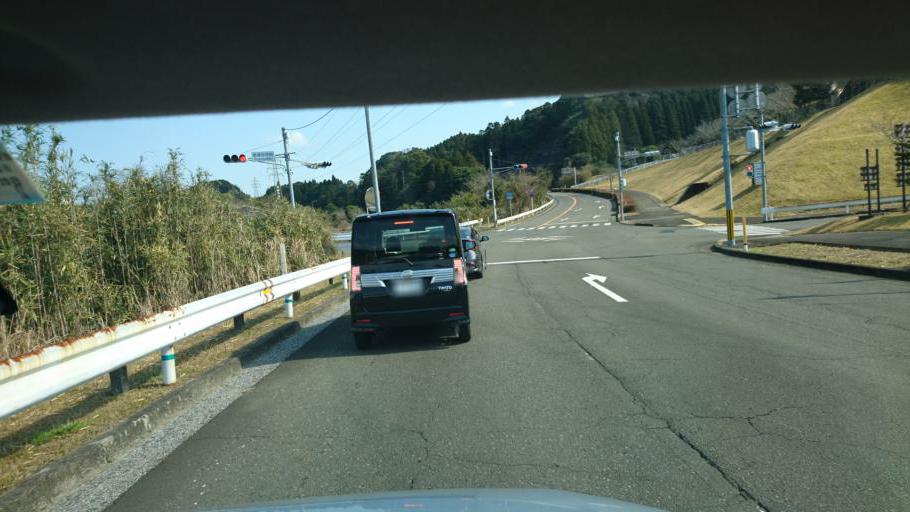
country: JP
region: Miyazaki
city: Miyazaki-shi
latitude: 31.8363
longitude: 131.4012
